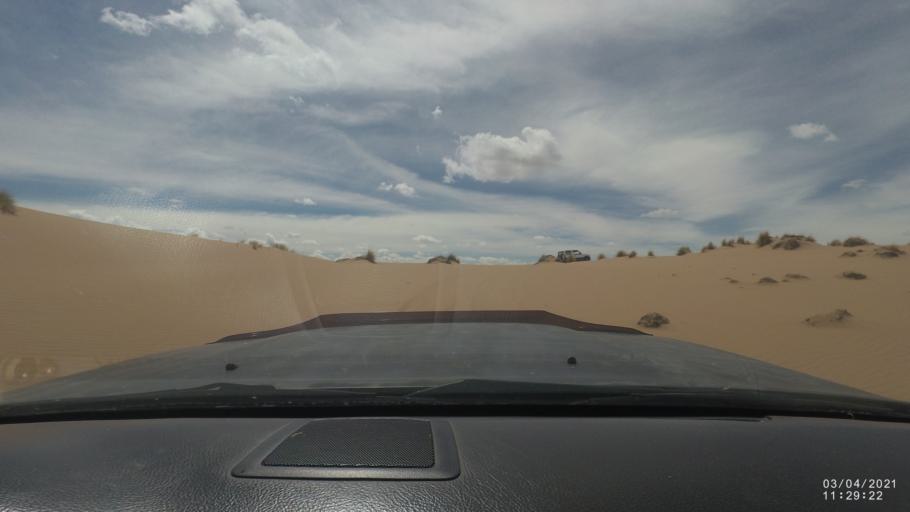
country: BO
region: Oruro
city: Poopo
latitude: -18.7025
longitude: -67.5091
